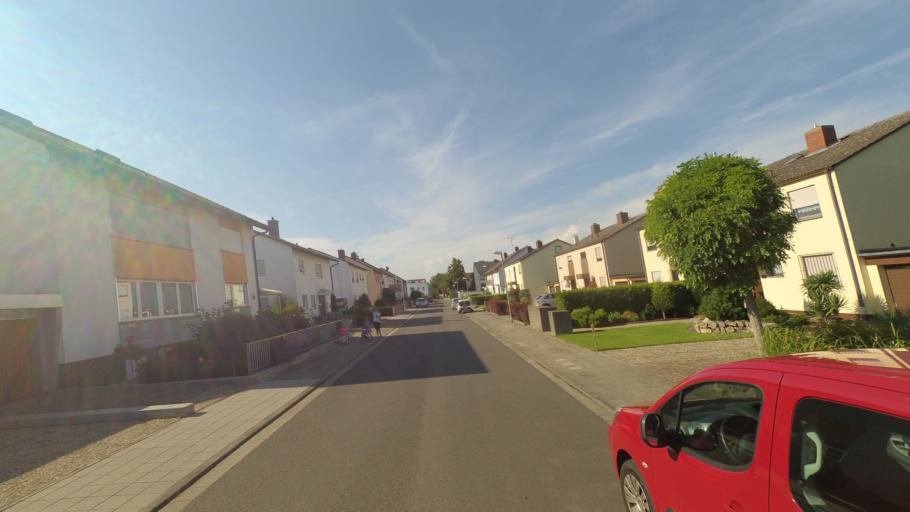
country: DE
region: Rheinland-Pfalz
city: Frankenthal
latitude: 49.5071
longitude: 8.3590
